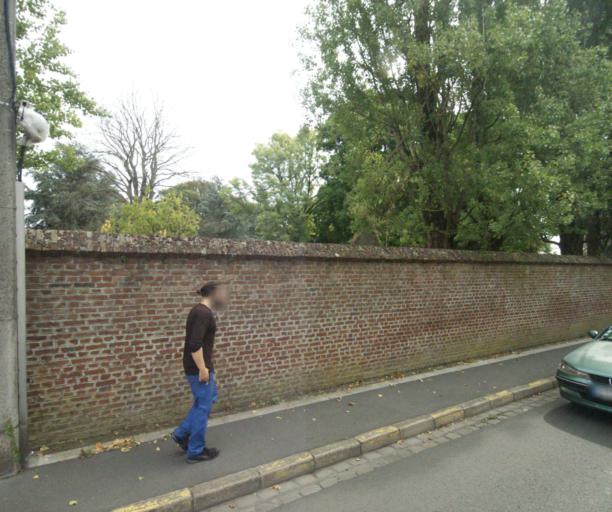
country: FR
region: Nord-Pas-de-Calais
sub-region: Departement du Nord
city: Wattignies
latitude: 50.6093
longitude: 3.0473
